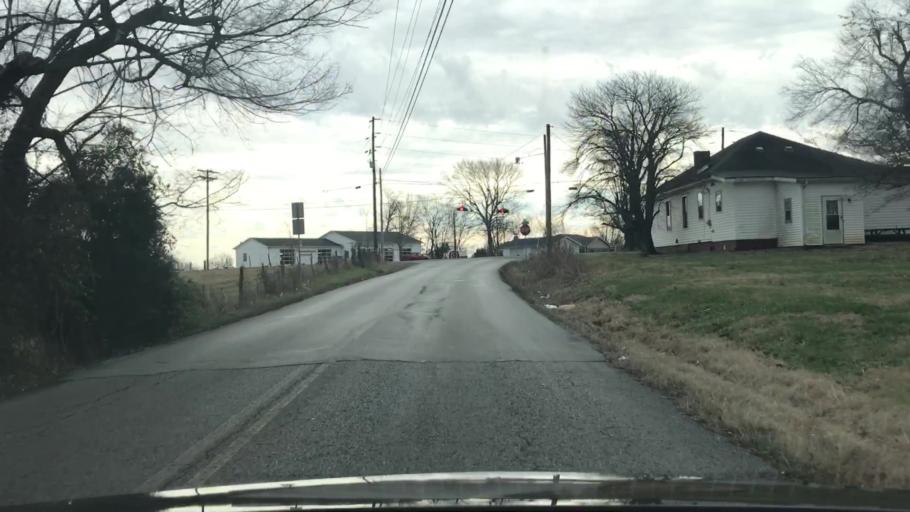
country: US
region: Kentucky
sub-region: Christian County
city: Hopkinsville
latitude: 36.8631
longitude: -87.5378
